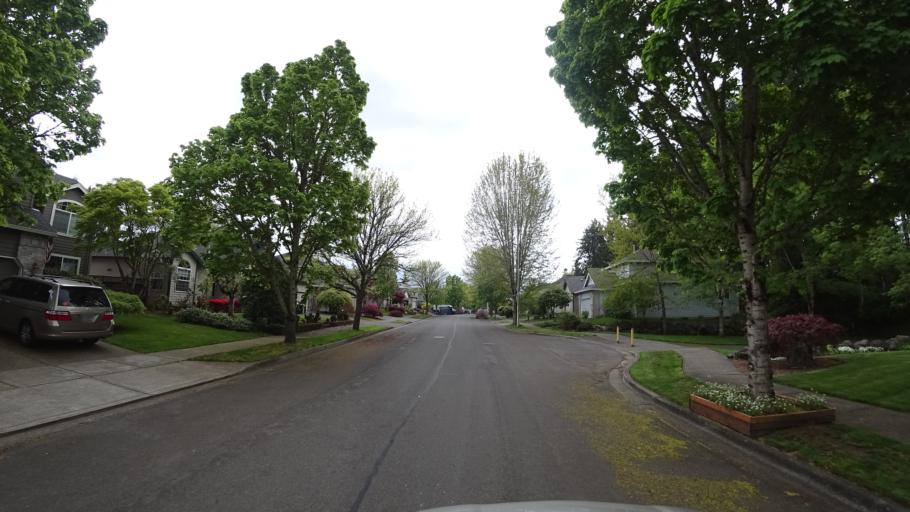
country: US
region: Oregon
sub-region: Washington County
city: Rockcreek
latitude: 45.5401
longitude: -122.9310
